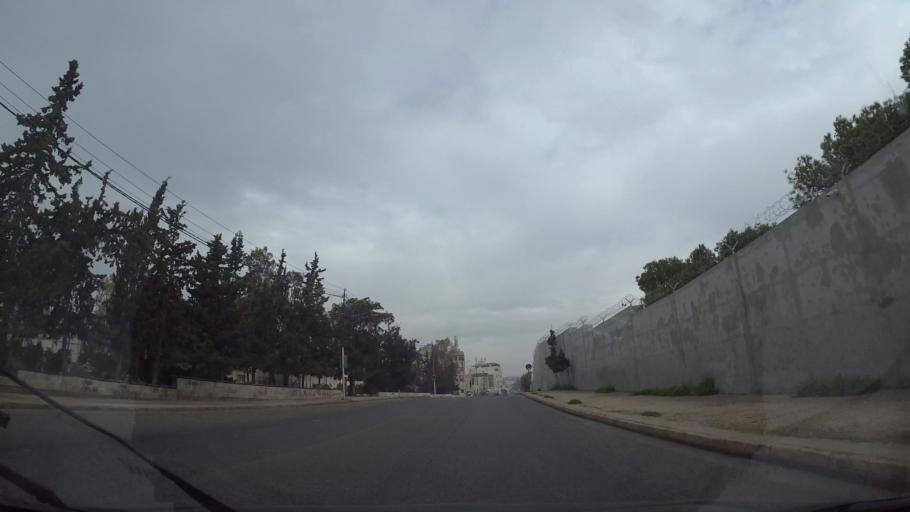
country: JO
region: Amman
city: Amman
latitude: 31.9627
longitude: 35.9378
